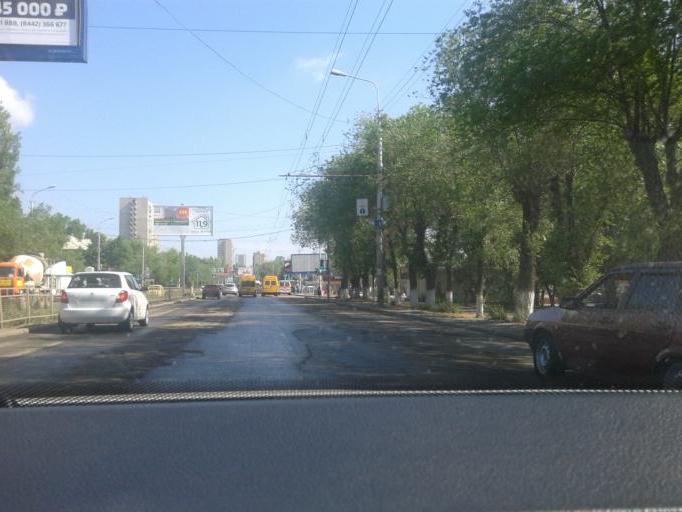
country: RU
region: Volgograd
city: Volgograd
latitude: 48.6115
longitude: 44.4226
